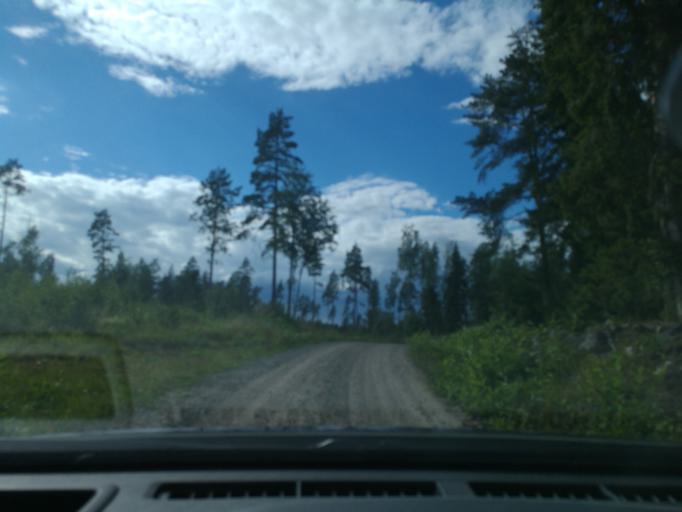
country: SE
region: Vaestmanland
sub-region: Surahammars Kommun
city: Ramnas
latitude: 59.7888
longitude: 16.2992
